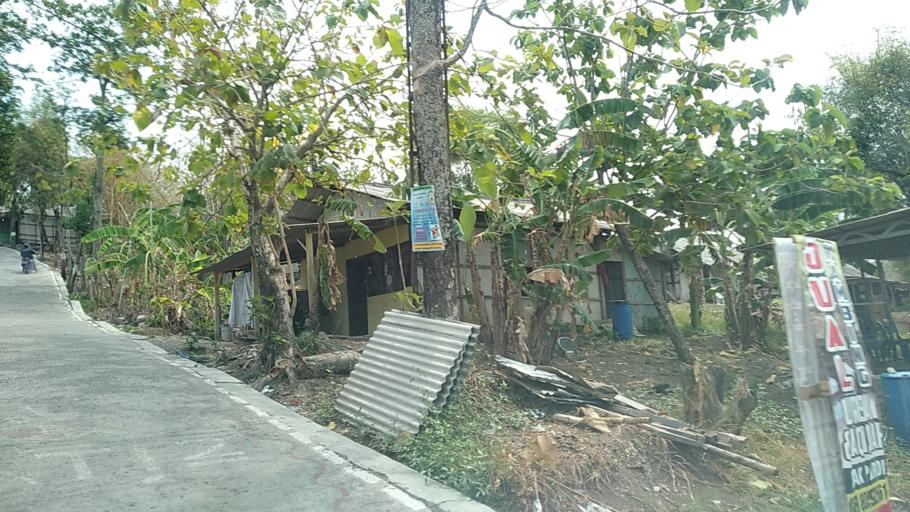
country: ID
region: Central Java
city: Semarang
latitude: -7.0394
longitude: 110.4406
